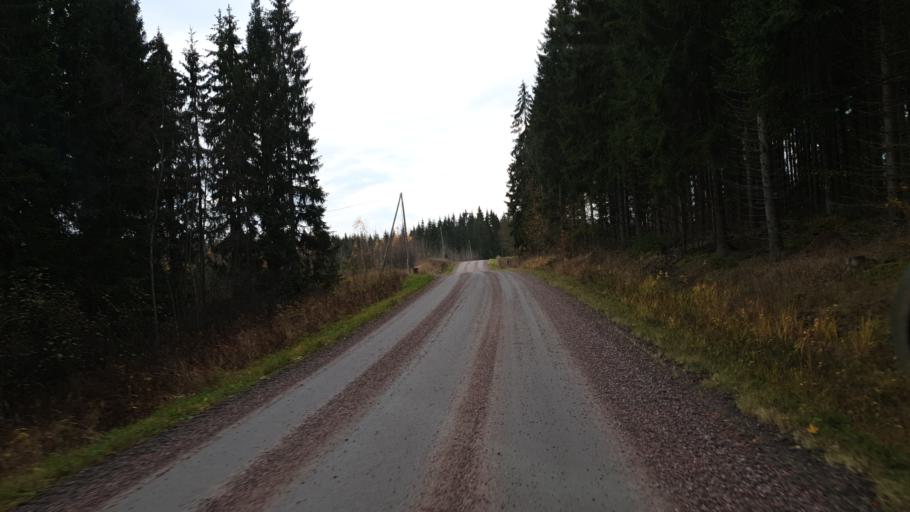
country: FI
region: Uusimaa
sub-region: Helsinki
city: Siuntio
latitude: 60.1510
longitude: 24.2763
